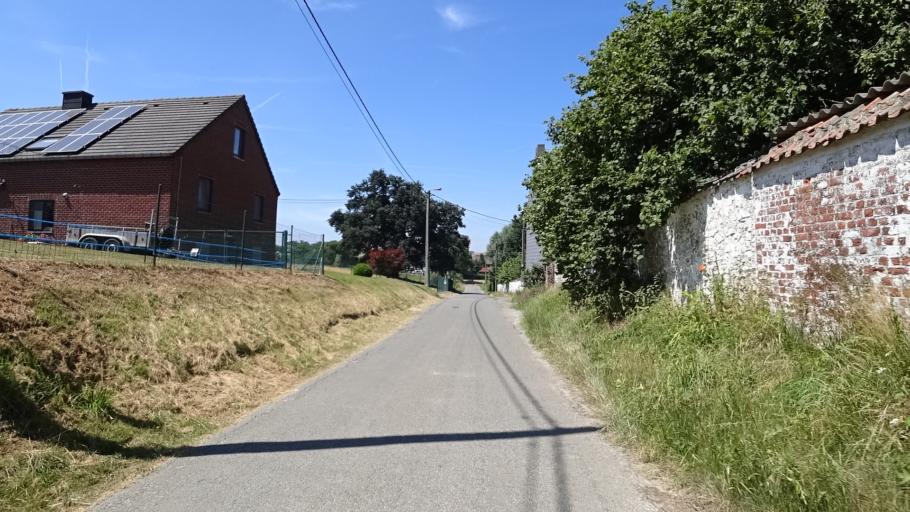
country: BE
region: Wallonia
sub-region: Province du Brabant Wallon
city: Incourt
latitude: 50.6690
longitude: 4.8332
